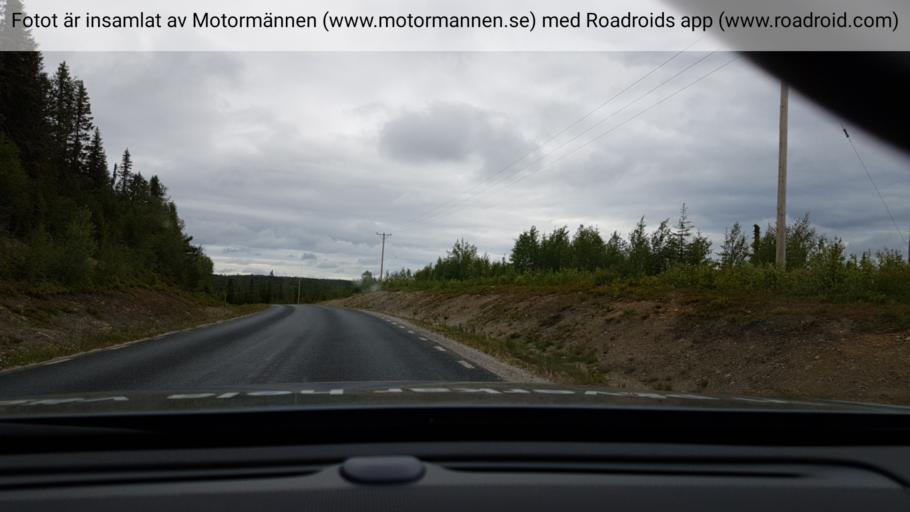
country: SE
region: Vaesterbotten
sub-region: Lycksele Kommun
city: Soderfors
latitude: 64.3838
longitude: 17.9976
